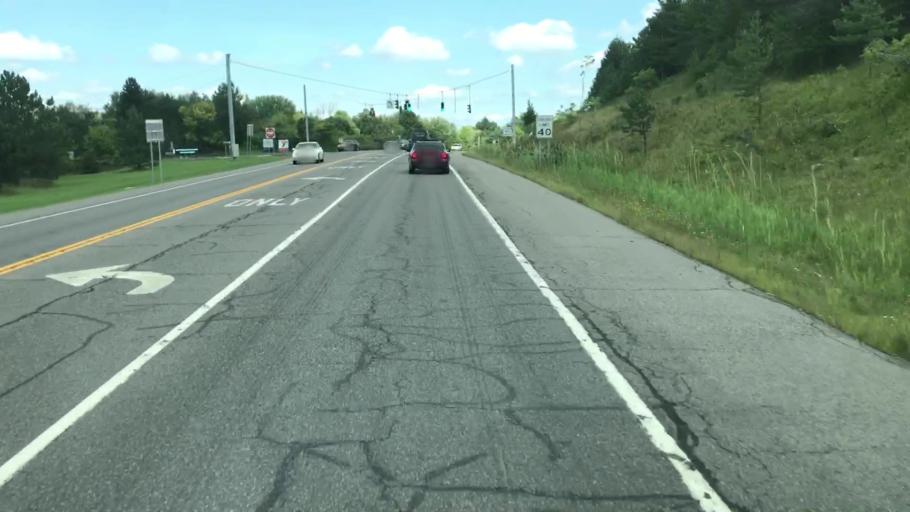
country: US
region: New York
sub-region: Onondaga County
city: Westvale
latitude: 43.0012
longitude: -76.1950
